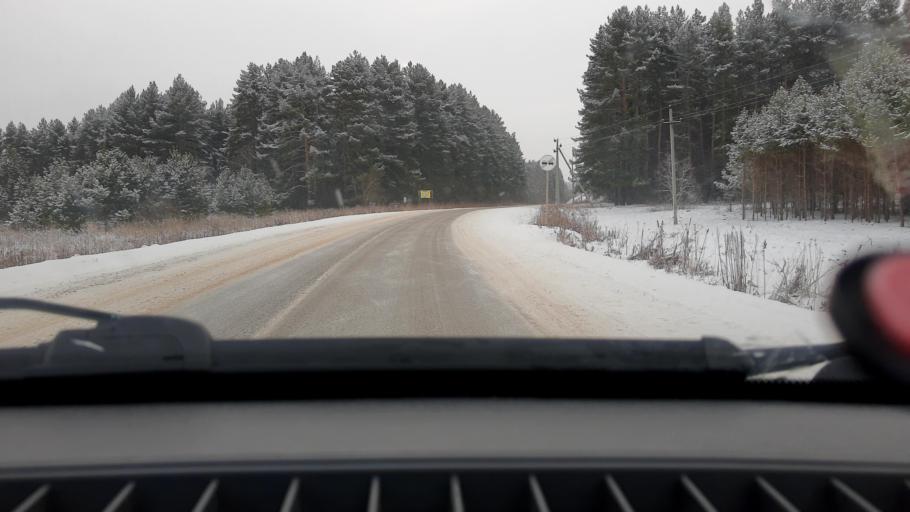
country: RU
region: Bashkortostan
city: Iglino
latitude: 54.6798
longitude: 56.4172
